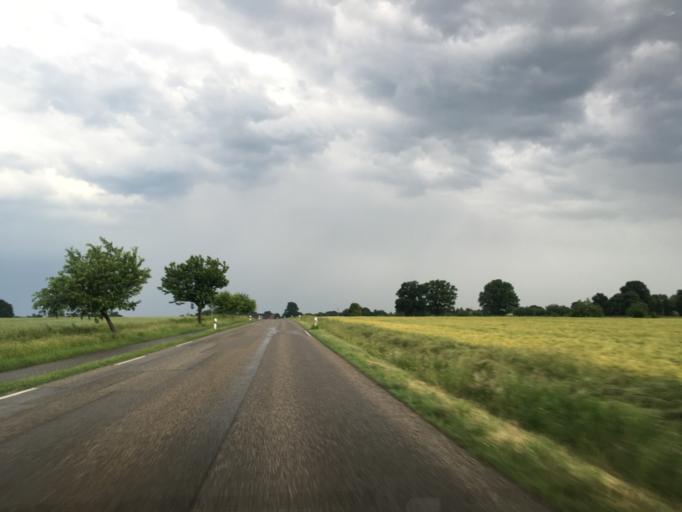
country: DE
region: North Rhine-Westphalia
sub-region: Regierungsbezirk Munster
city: Nordwalde
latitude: 52.0743
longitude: 7.4791
